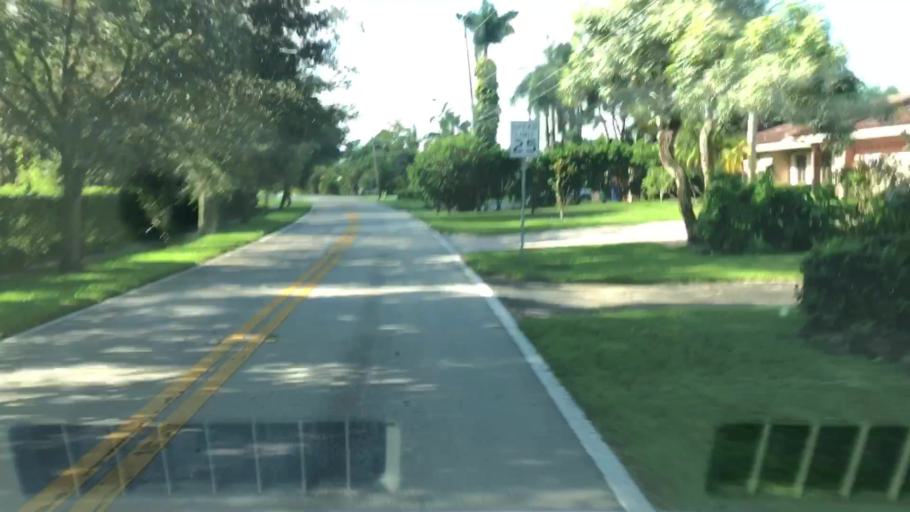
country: US
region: Florida
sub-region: Broward County
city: Coral Springs
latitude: 26.2782
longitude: -80.2565
